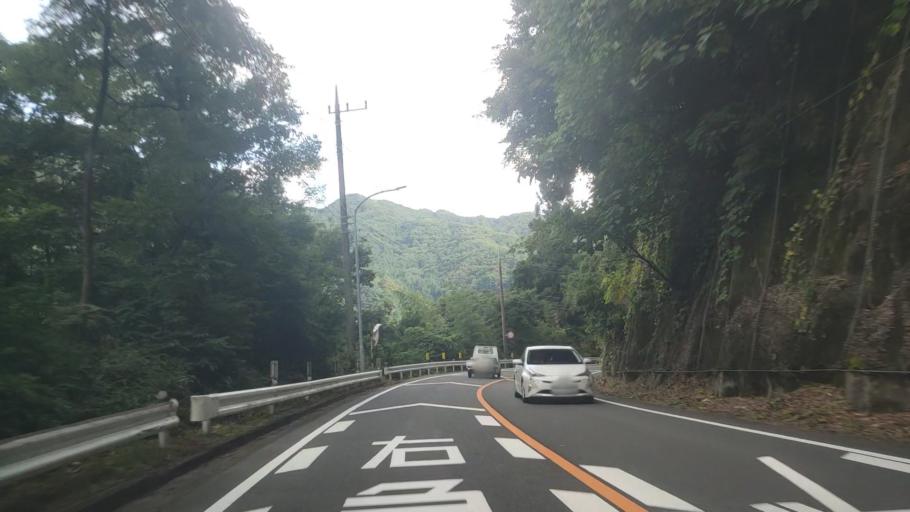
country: JP
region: Gunma
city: Omamacho-omama
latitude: 36.5705
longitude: 139.3787
